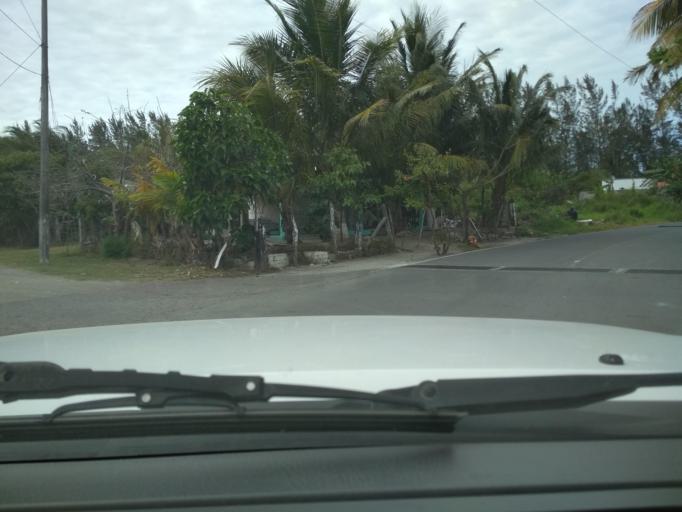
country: MX
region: Veracruz
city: Anton Lizardo
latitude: 19.0377
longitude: -95.9701
